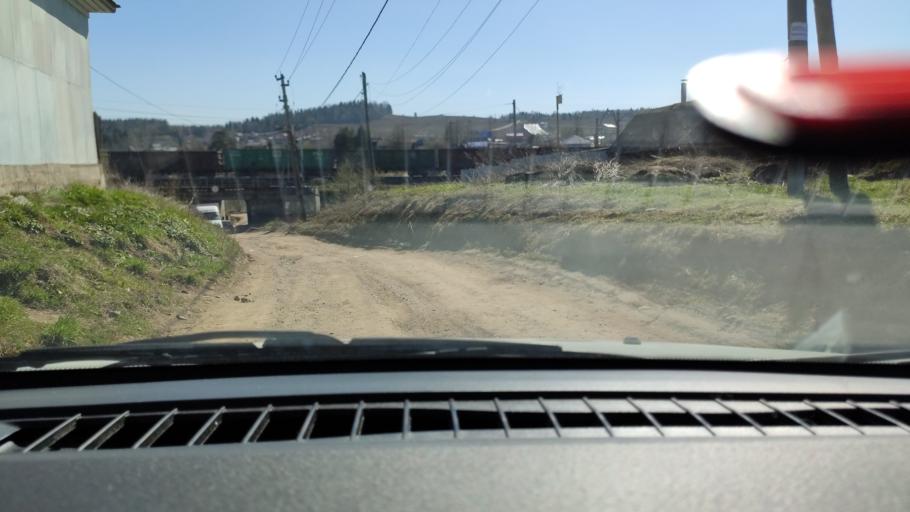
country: RU
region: Perm
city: Bershet'
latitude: 57.7280
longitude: 56.3784
